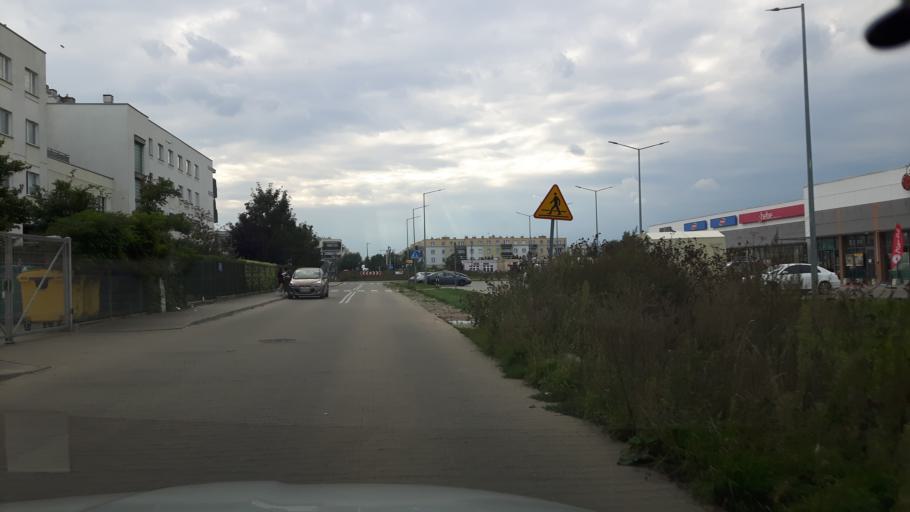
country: PL
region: Masovian Voivodeship
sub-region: Warszawa
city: Targowek
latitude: 52.3156
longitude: 21.0631
